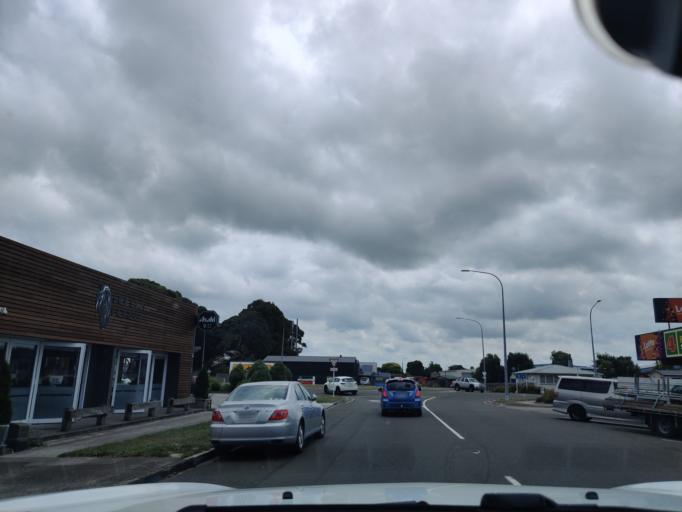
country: NZ
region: Manawatu-Wanganui
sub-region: Palmerston North City
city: Palmerston North
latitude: -40.3514
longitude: 175.5852
